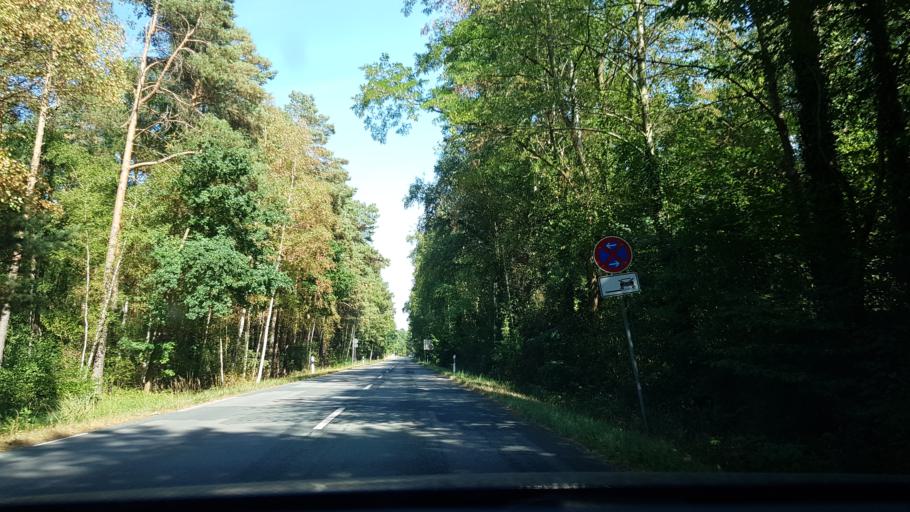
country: DE
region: Lower Saxony
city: Isenbuttel
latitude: 52.4587
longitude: 10.6114
